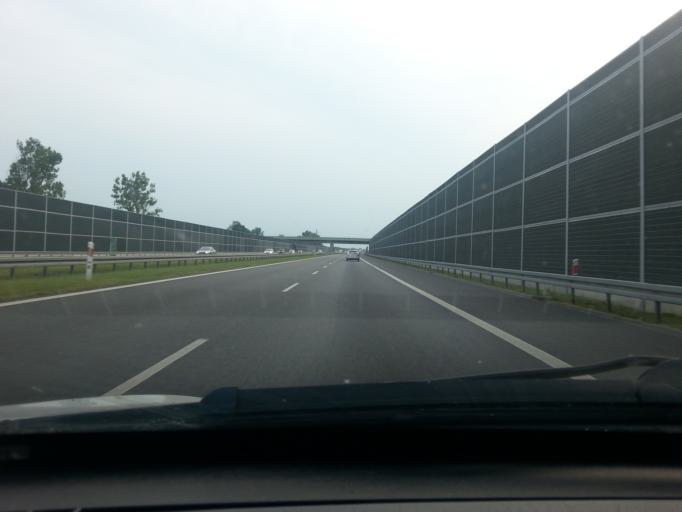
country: PL
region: Masovian Voivodeship
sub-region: Powiat zyrardowski
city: Wiskitki
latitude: 52.1032
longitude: 20.4318
